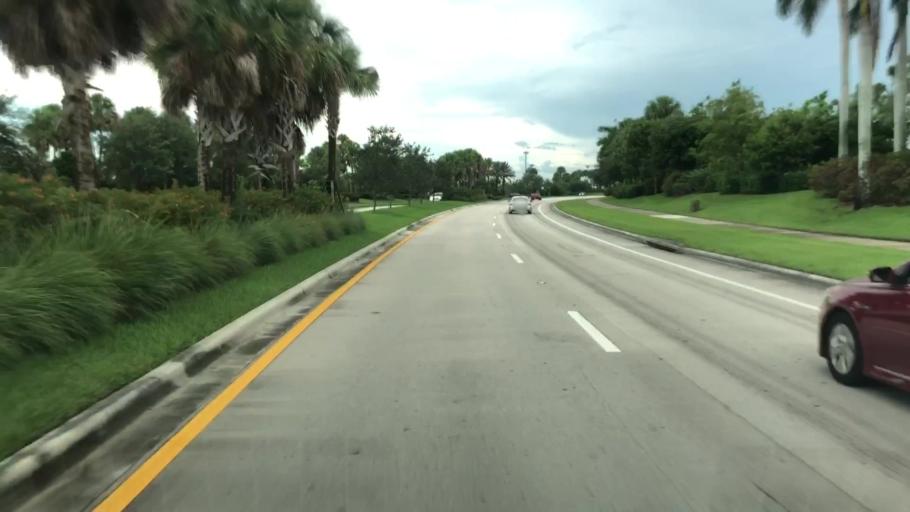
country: US
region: Florida
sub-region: Broward County
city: Parkland
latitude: 26.3308
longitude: -80.2679
